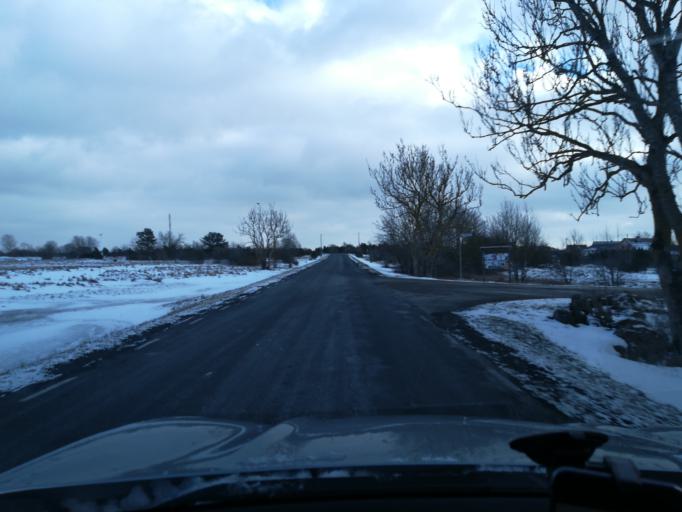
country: EE
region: Harju
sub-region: Harku vald
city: Tabasalu
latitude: 59.4336
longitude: 24.4027
